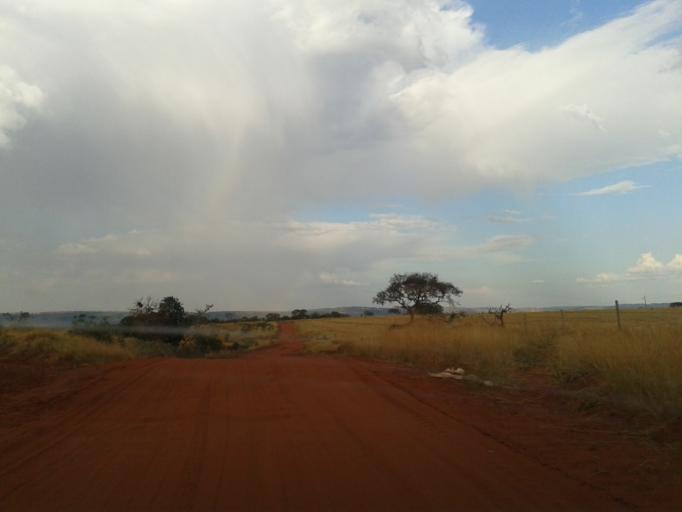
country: BR
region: Minas Gerais
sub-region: Santa Vitoria
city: Santa Vitoria
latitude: -19.1903
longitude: -49.8723
